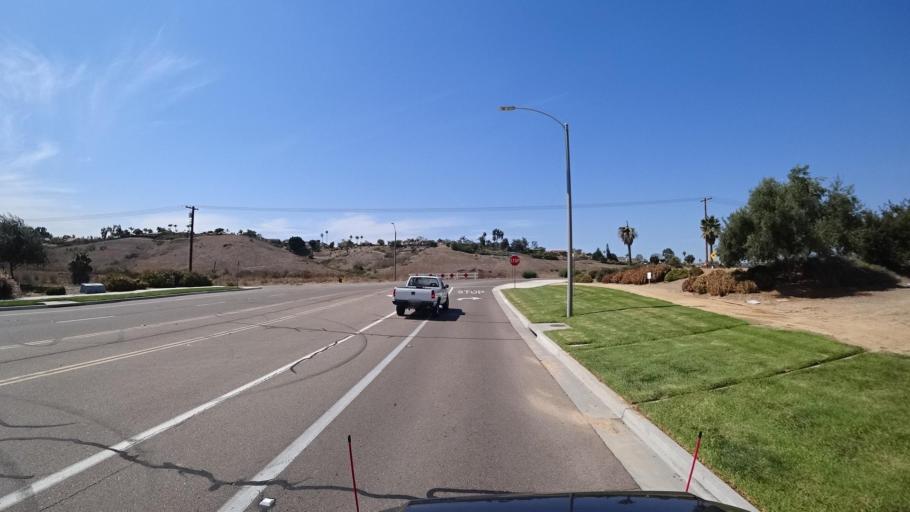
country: US
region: California
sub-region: San Diego County
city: La Presa
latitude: 32.6722
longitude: -116.9967
